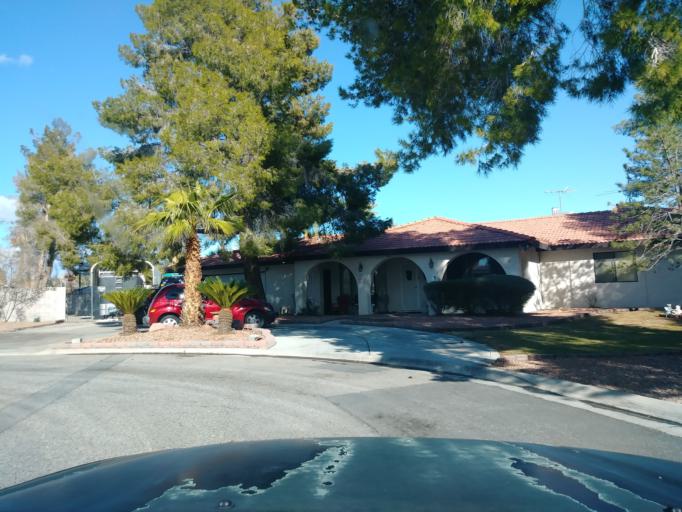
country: US
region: Nevada
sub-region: Clark County
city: Spring Valley
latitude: 36.1504
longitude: -115.2227
